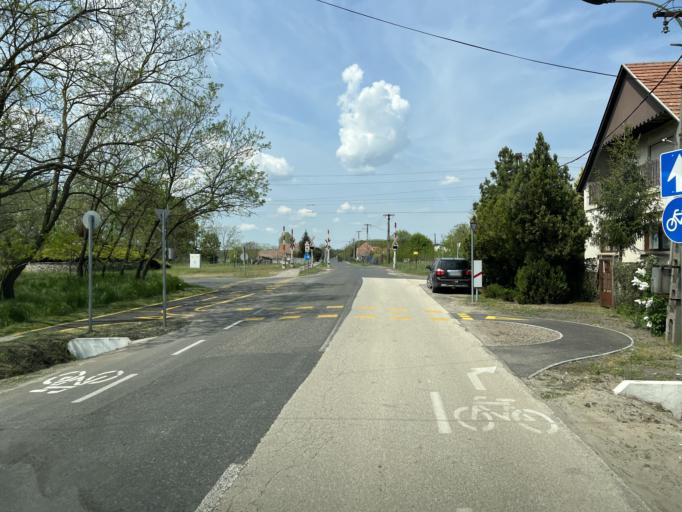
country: HU
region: Pest
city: Cegled
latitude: 47.1033
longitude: 19.7948
